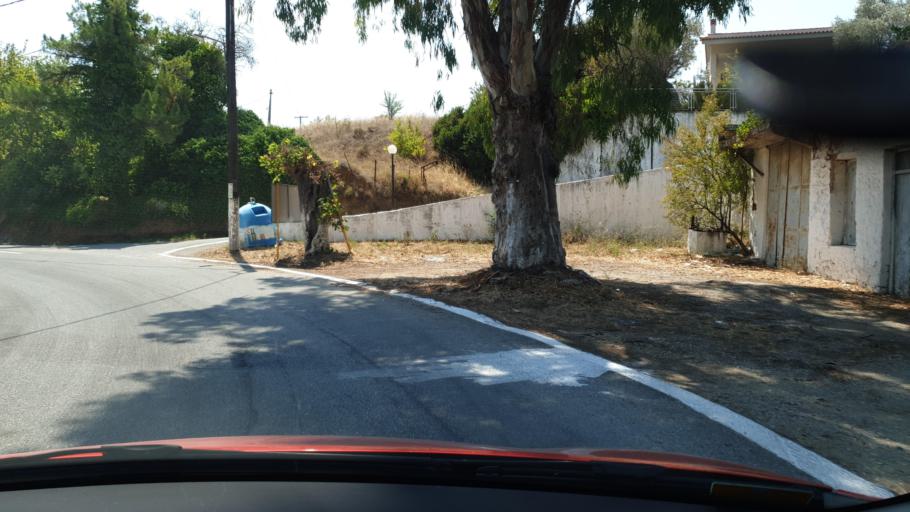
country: GR
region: Central Greece
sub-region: Nomos Evvoias
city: Oxilithos
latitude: 38.5284
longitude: 24.0876
